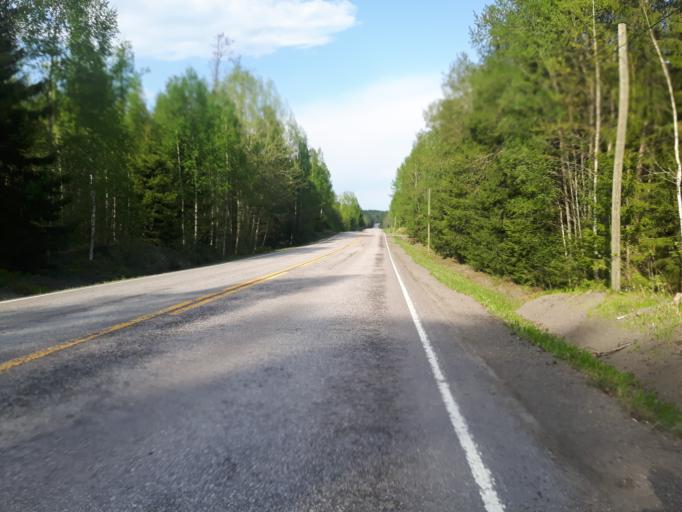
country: FI
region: Uusimaa
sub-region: Porvoo
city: Porvoo
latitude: 60.4750
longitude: 25.7977
